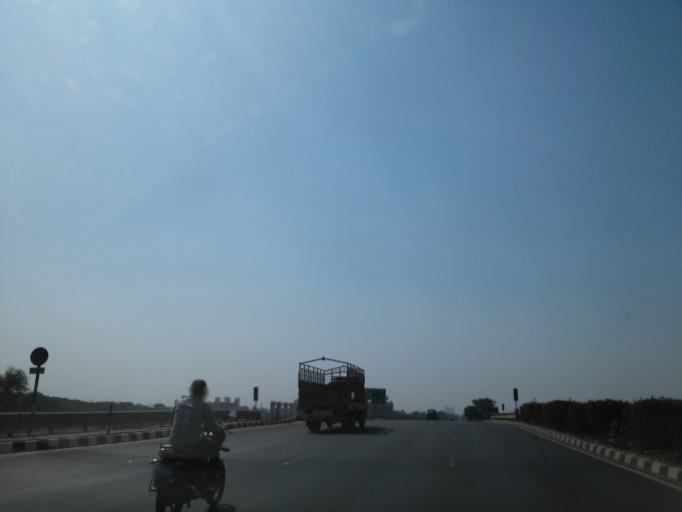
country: IN
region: Gujarat
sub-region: Gandhinagar
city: Adalaj
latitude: 23.1741
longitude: 72.5806
